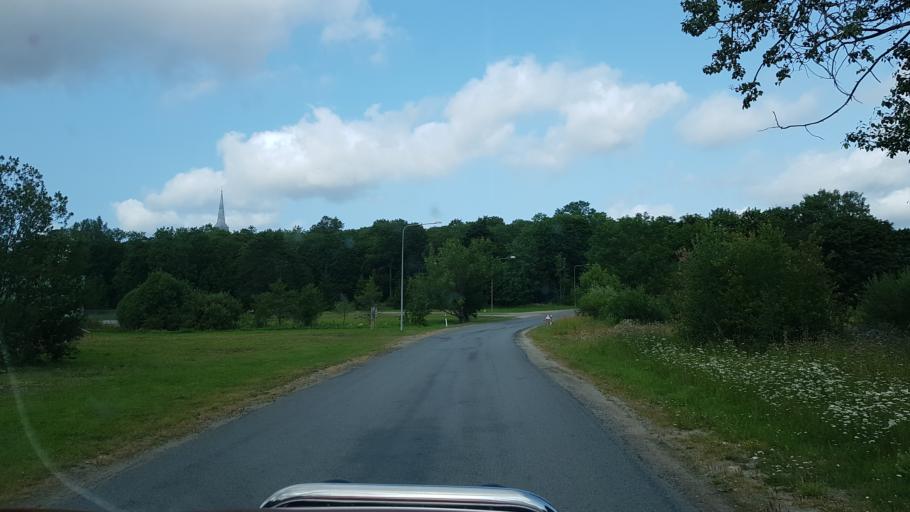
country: EE
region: Laeaene-Virumaa
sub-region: Kadrina vald
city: Kadrina
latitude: 59.3404
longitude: 26.1268
